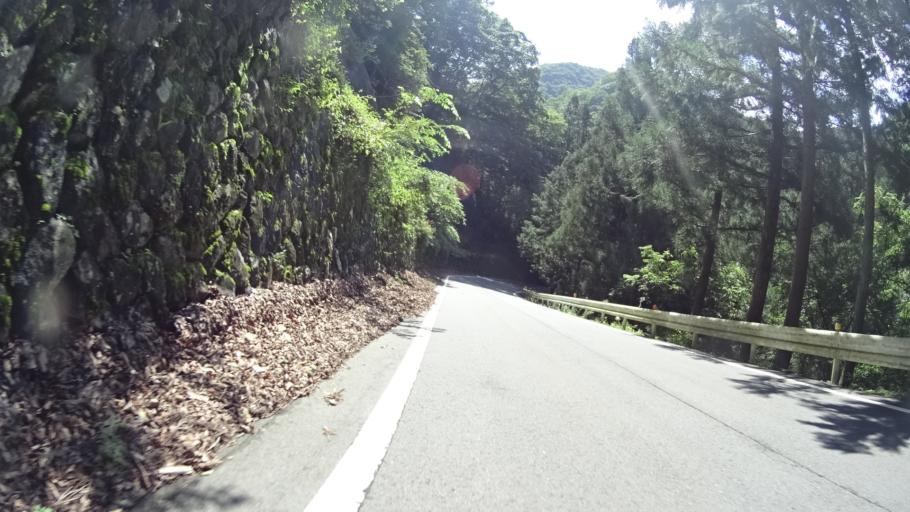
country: JP
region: Gunma
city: Tomioka
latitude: 36.0613
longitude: 138.8380
